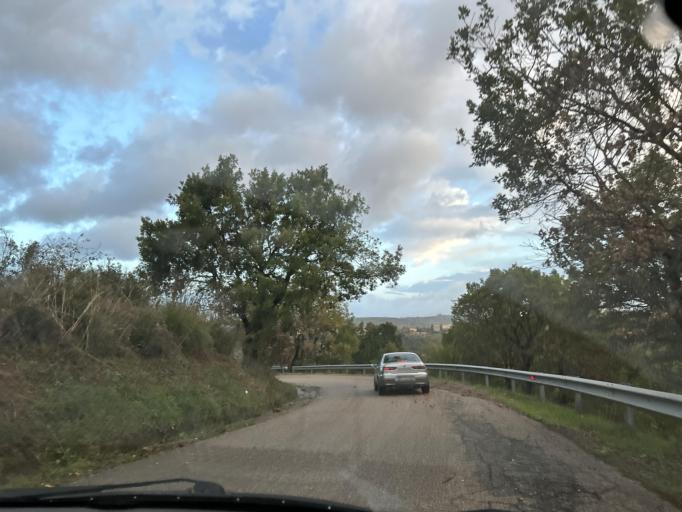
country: IT
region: Calabria
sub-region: Provincia di Catanzaro
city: Squillace
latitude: 38.7696
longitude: 16.5107
